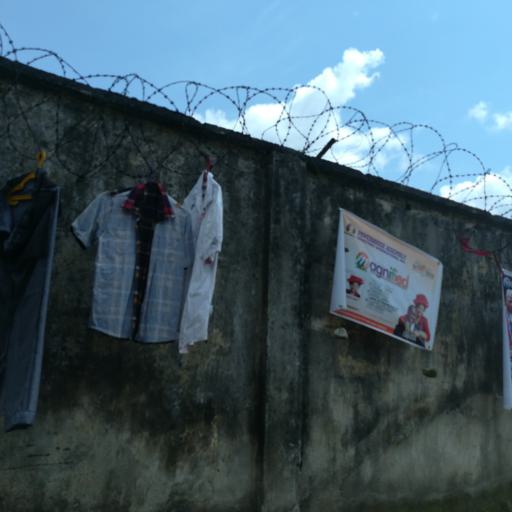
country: NG
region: Rivers
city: Okrika
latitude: 4.7779
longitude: 7.0610
